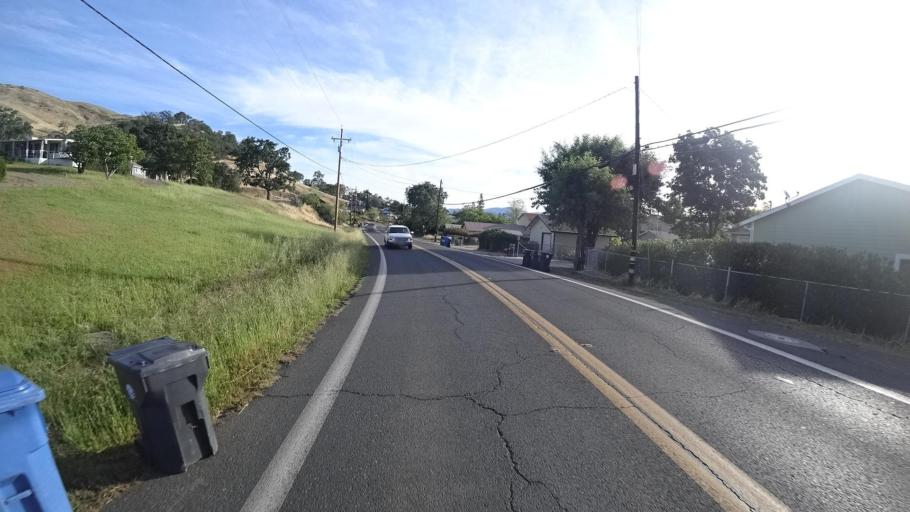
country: US
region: California
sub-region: Lake County
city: North Lakeport
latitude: 39.0823
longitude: -122.9045
